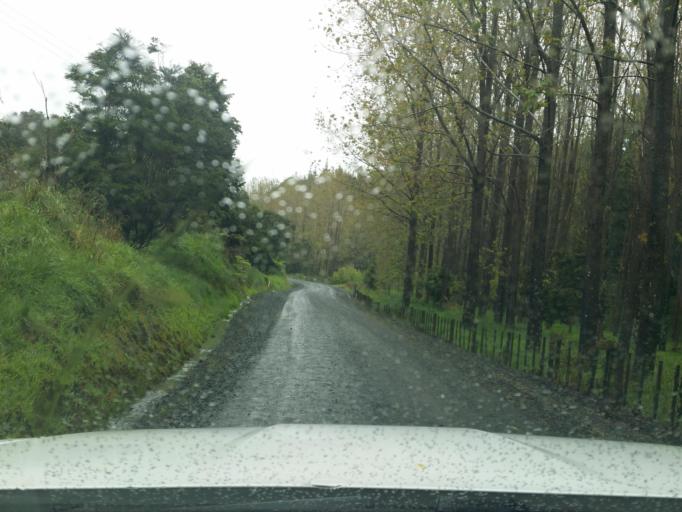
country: NZ
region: Northland
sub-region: Kaipara District
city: Dargaville
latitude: -35.8049
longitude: 173.9960
